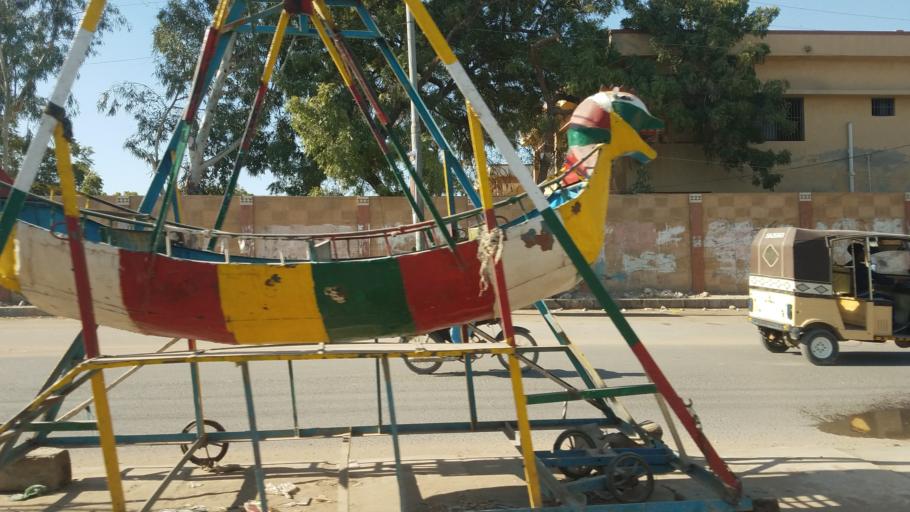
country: PK
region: Sindh
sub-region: Karachi District
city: Karachi
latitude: 24.9200
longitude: 67.0520
